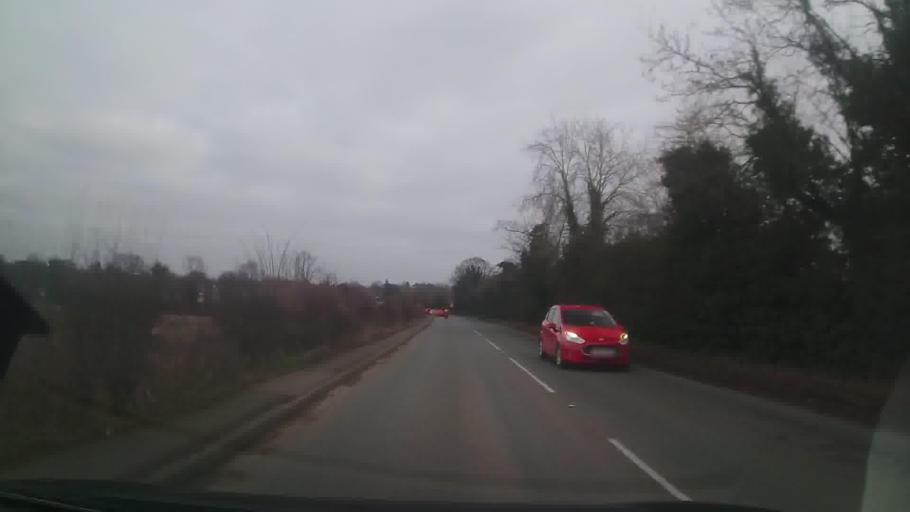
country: GB
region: England
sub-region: Shropshire
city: Bicton
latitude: 52.7268
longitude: -2.8248
